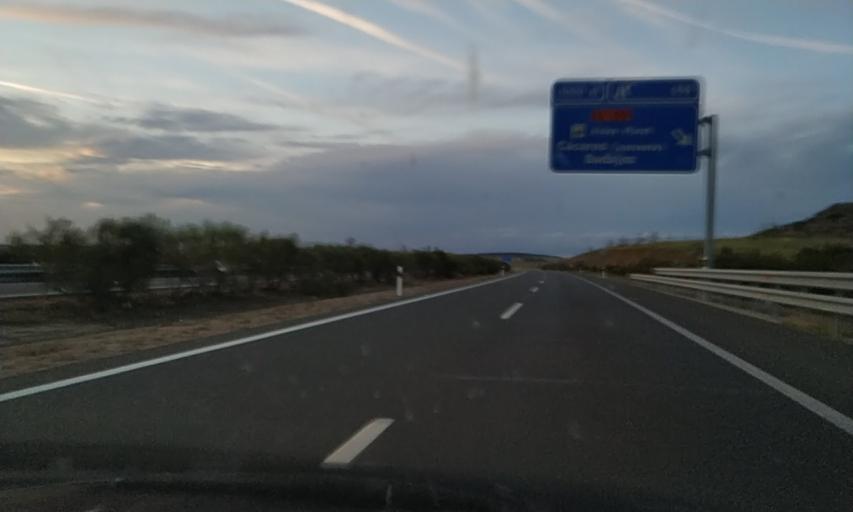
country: ES
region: Extremadura
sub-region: Provincia de Caceres
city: Caceres
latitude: 39.4191
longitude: -6.4017
